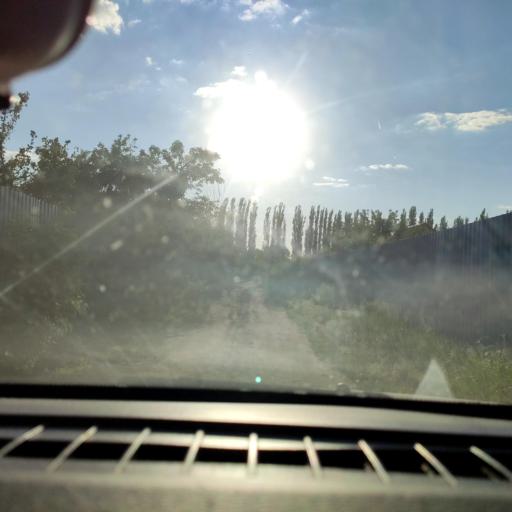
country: RU
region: Voronezj
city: Maslovka
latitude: 51.5209
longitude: 39.2286
